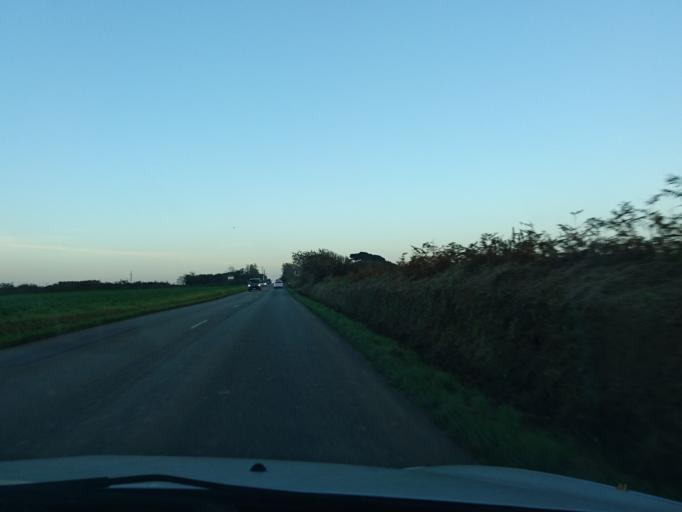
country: FR
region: Brittany
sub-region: Departement du Finistere
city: Lanrivoare
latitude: 48.4633
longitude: -4.6356
